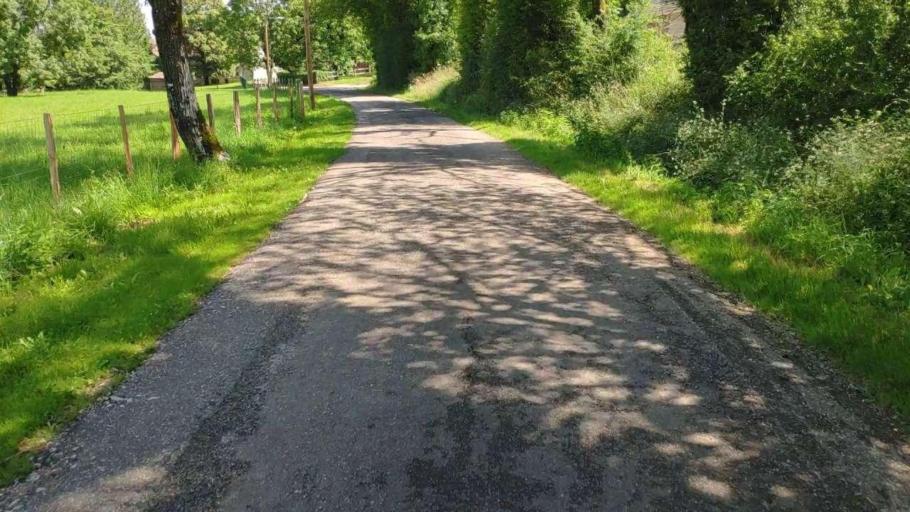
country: FR
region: Franche-Comte
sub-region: Departement du Jura
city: Bletterans
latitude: 46.8264
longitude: 5.5576
